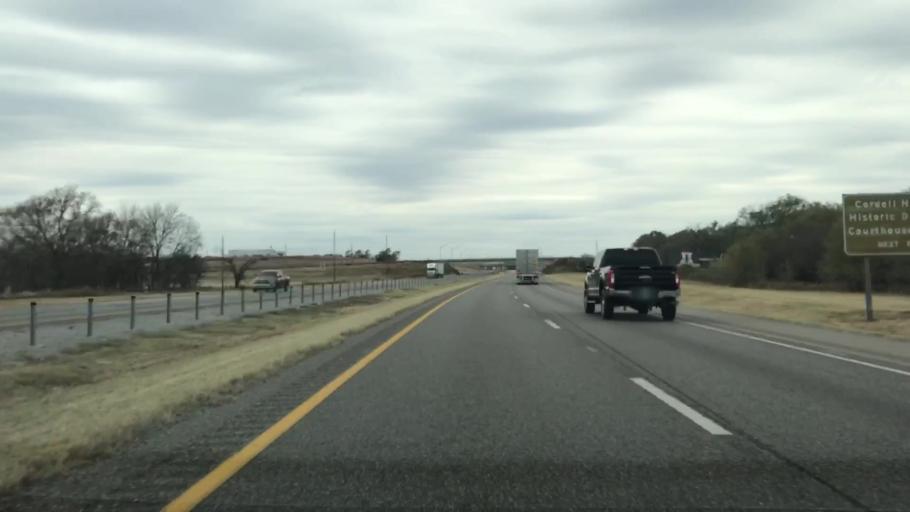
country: US
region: Oklahoma
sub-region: Custer County
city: Clinton
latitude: 35.5001
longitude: -98.9544
